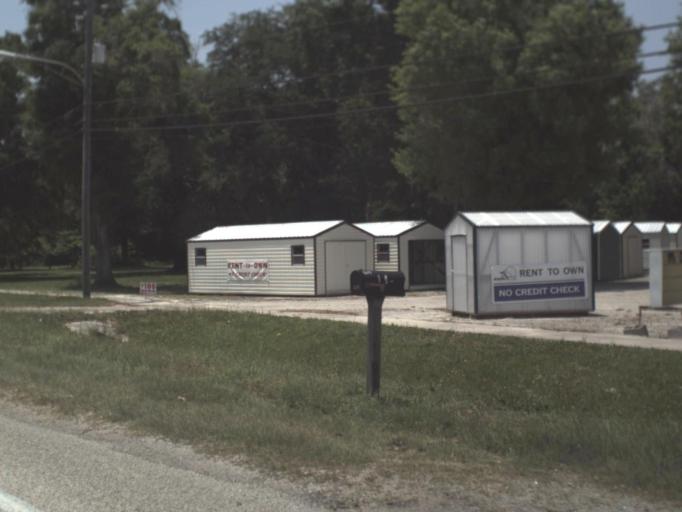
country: US
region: Florida
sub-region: Bradford County
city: Starke
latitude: 29.9305
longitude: -82.1197
